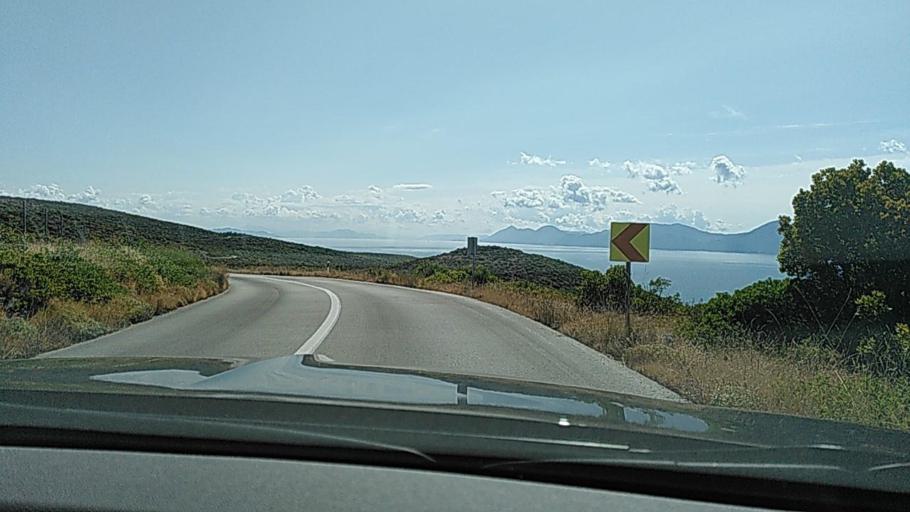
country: HR
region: Splitsko-Dalmatinska
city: Tucepi
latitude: 43.1264
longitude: 17.0915
